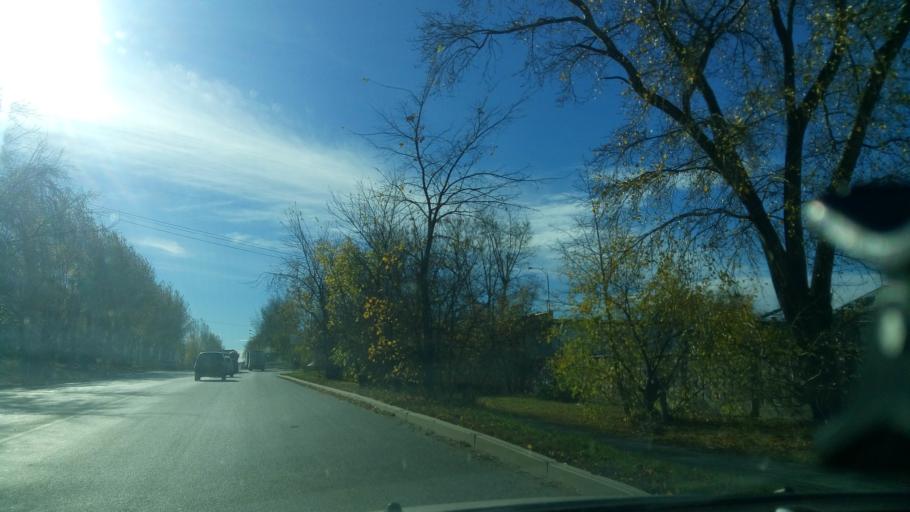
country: RU
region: Sverdlovsk
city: Sovkhoznyy
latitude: 56.7687
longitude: 60.6285
